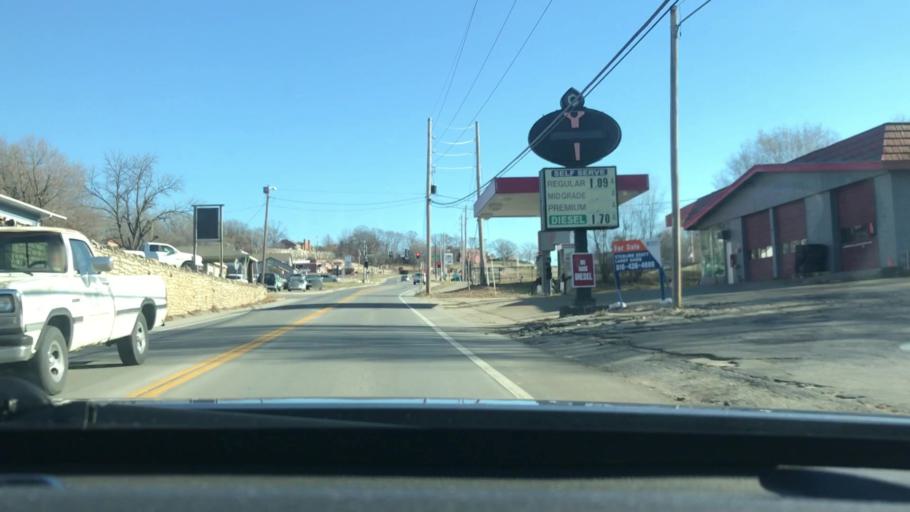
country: US
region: Missouri
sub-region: Platte County
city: Platte City
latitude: 39.3673
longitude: -94.7818
